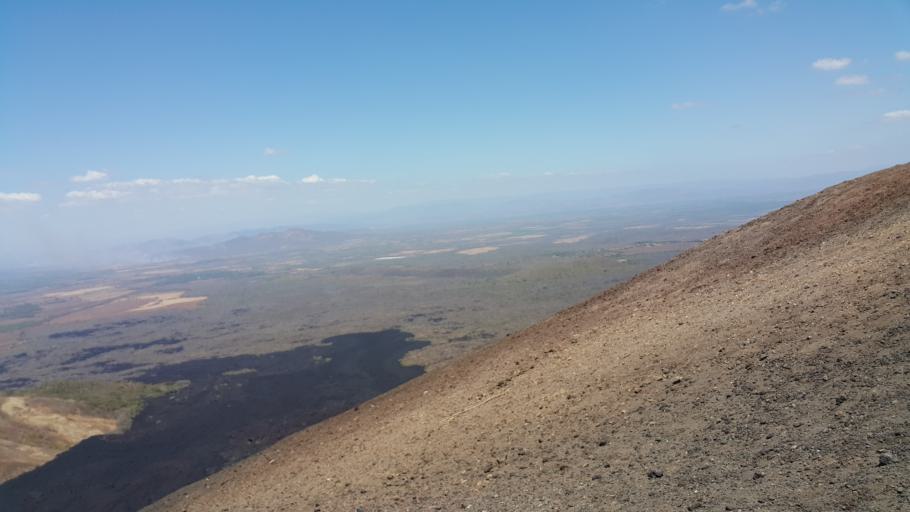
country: NI
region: Leon
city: Telica
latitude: 12.5078
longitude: -86.7038
